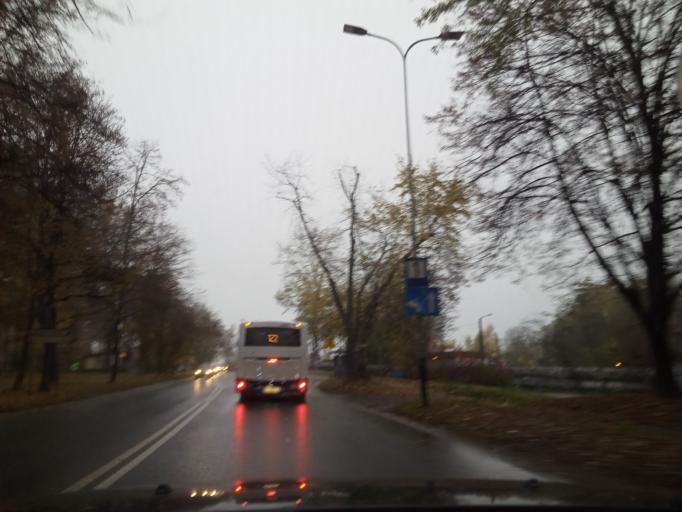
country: PL
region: Lesser Poland Voivodeship
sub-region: Powiat wielicki
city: Kokotow
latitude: 50.0944
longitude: 20.0642
